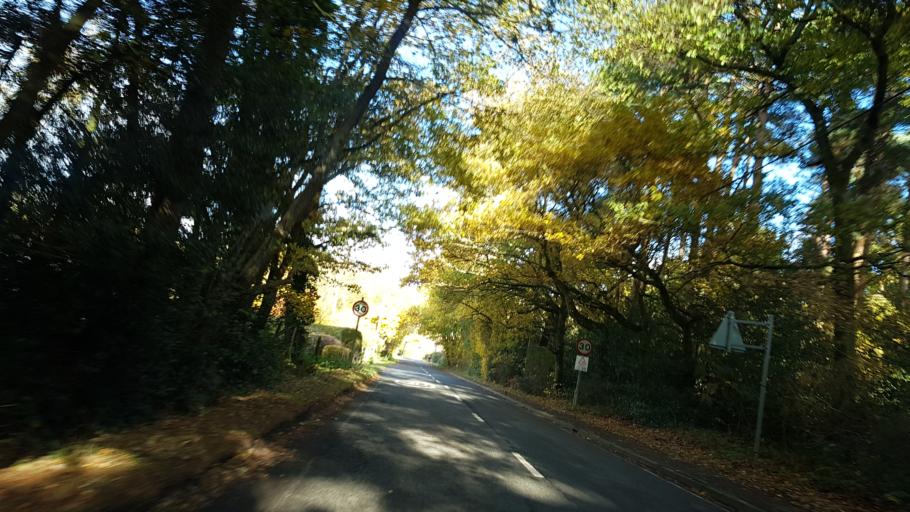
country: GB
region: England
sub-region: Surrey
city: Elstead
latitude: 51.1736
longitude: -0.7132
